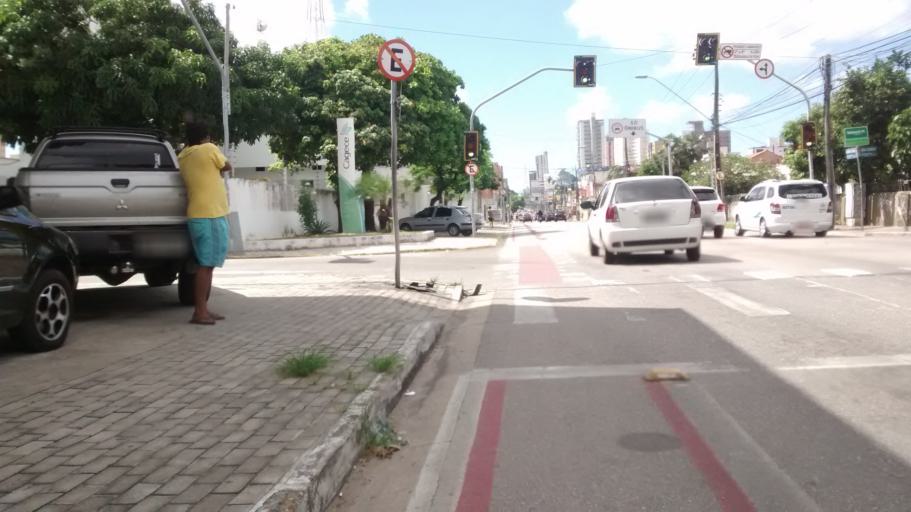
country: BR
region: Ceara
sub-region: Fortaleza
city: Fortaleza
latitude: -3.7405
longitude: -38.5182
